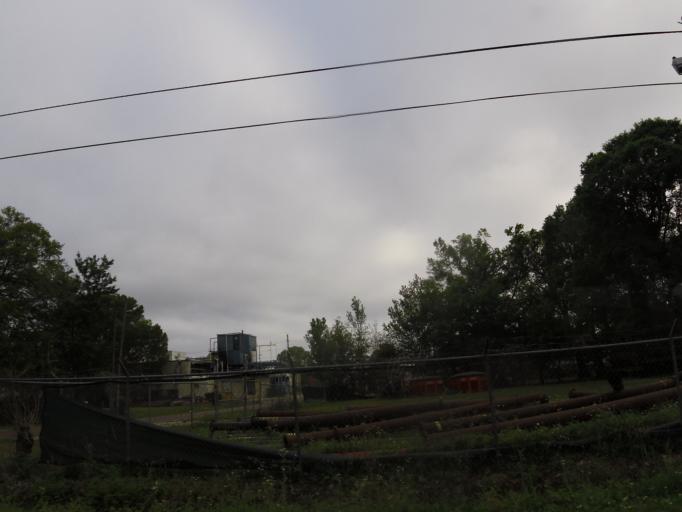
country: US
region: Florida
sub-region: Duval County
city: Jacksonville
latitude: 30.3238
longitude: -81.7264
